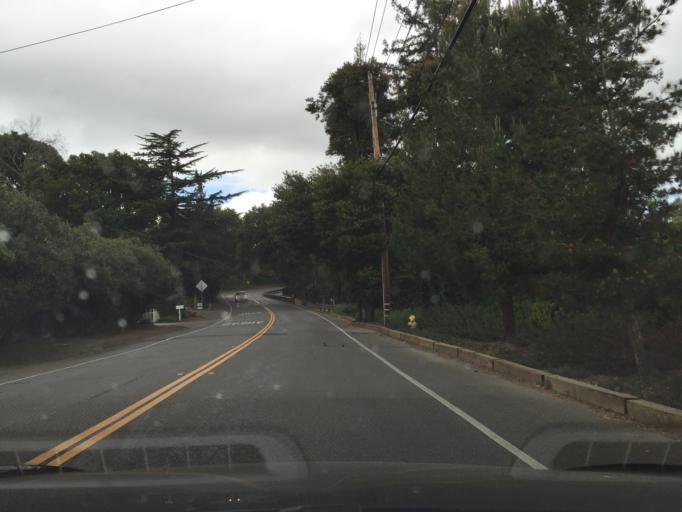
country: US
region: California
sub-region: Santa Clara County
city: Los Altos
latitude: 37.3806
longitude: -122.1248
